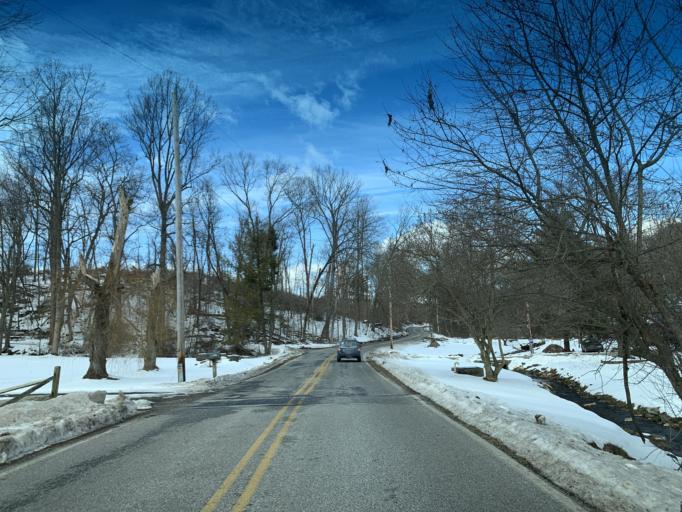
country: US
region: Pennsylvania
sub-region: York County
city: Shrewsbury
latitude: 39.7977
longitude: -76.6535
